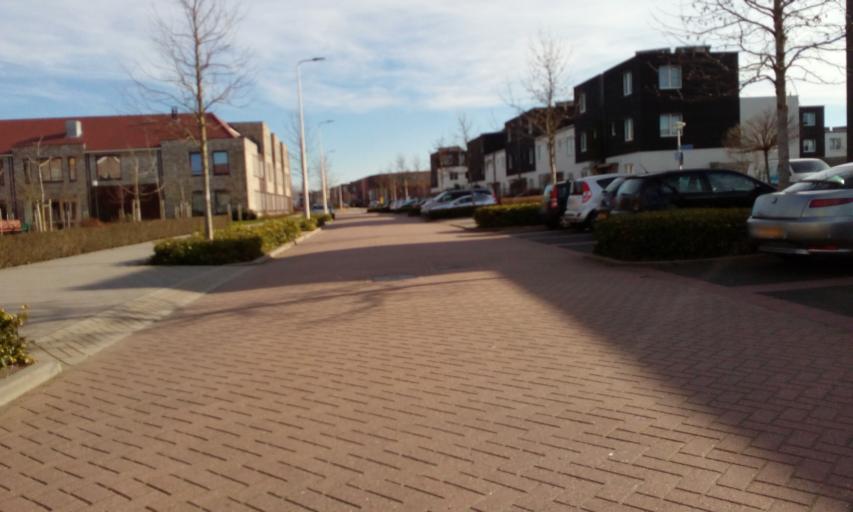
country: NL
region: South Holland
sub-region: Gemeente Alphen aan den Rijn
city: Alphen aan den Rijn
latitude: 52.1199
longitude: 4.6405
